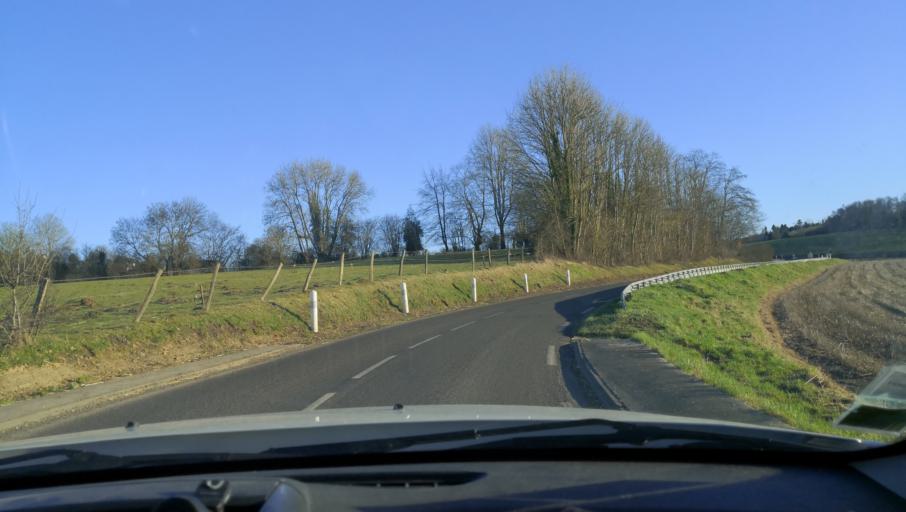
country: FR
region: Haute-Normandie
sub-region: Departement de la Seine-Maritime
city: Saint-Martin-Osmonville
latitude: 49.6119
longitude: 1.3276
